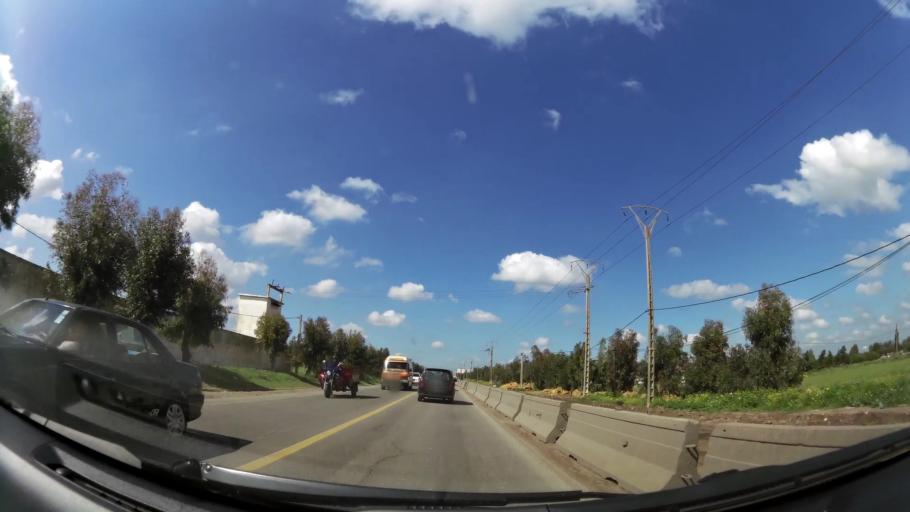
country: MA
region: Grand Casablanca
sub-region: Mediouna
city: Mediouna
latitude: 33.4360
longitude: -7.5205
